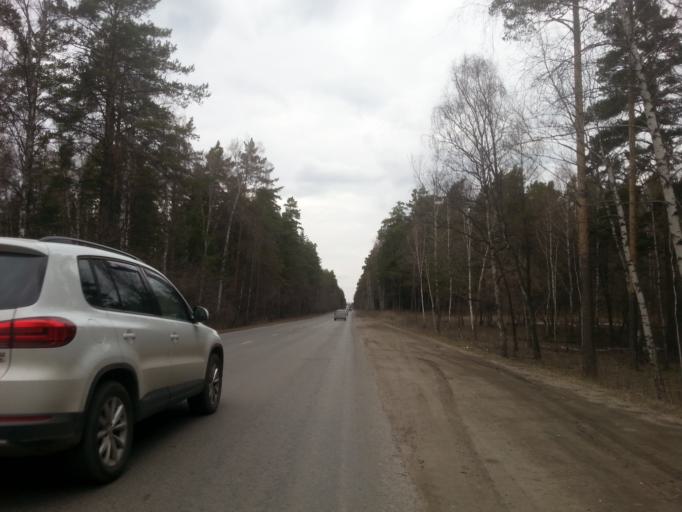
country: RU
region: Altai Krai
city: Yuzhnyy
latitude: 53.2767
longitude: 83.7199
